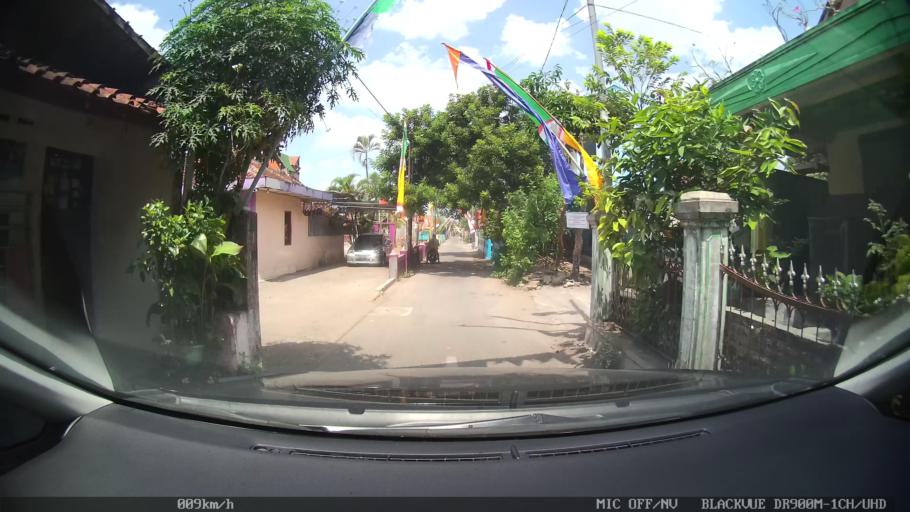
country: ID
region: Daerah Istimewa Yogyakarta
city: Kasihan
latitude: -7.8138
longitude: 110.3531
